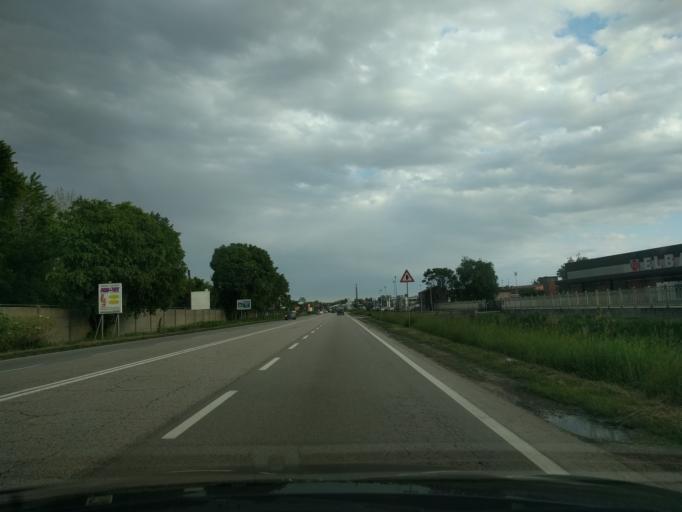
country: IT
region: Emilia-Romagna
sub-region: Provincia di Ferrara
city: Ferrara
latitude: 44.8551
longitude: 11.5846
